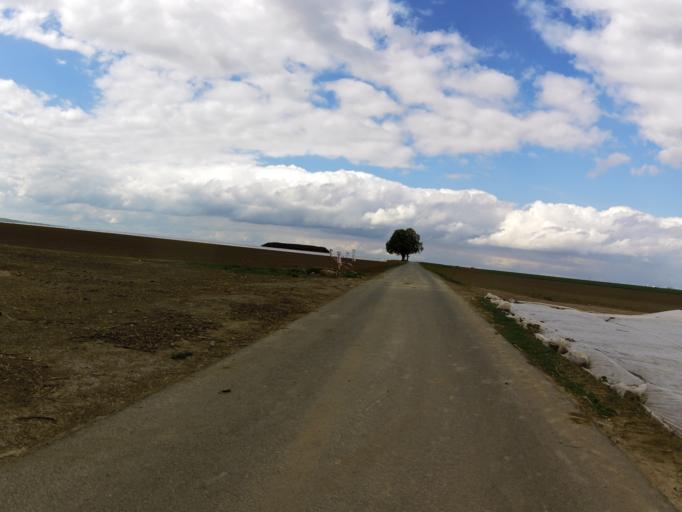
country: DE
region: Bavaria
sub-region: Regierungsbezirk Unterfranken
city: Oberpleichfeld
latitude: 49.8663
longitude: 10.0810
